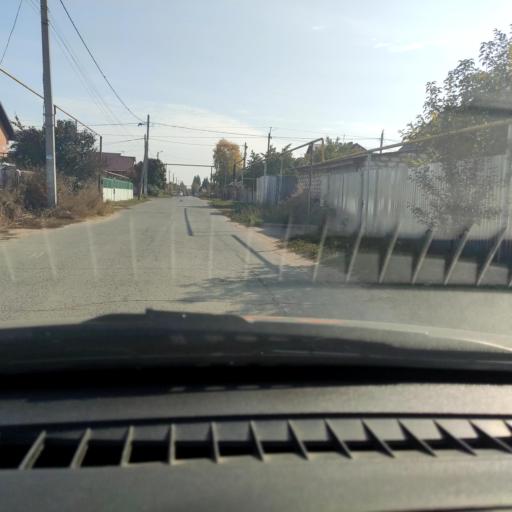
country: RU
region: Samara
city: Podstepki
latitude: 53.5140
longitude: 49.2332
